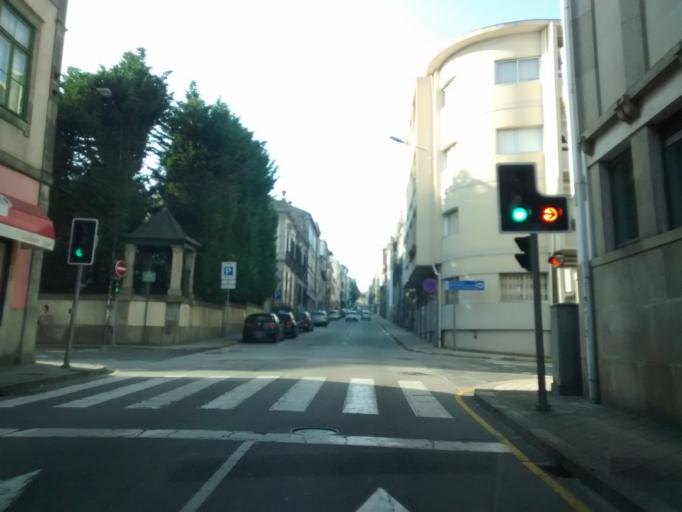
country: PT
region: Porto
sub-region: Porto
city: Porto
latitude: 41.1508
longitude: -8.6022
